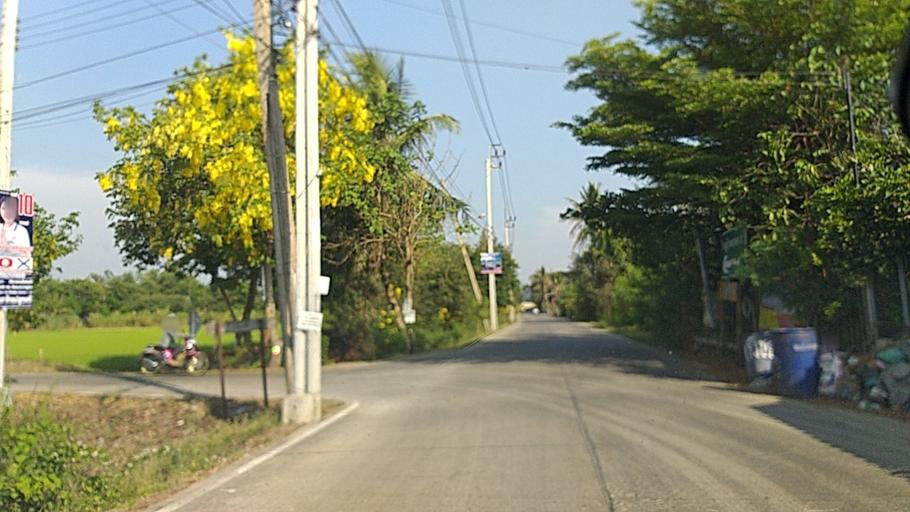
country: TH
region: Nonthaburi
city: Sai Noi
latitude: 13.9356
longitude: 100.3417
